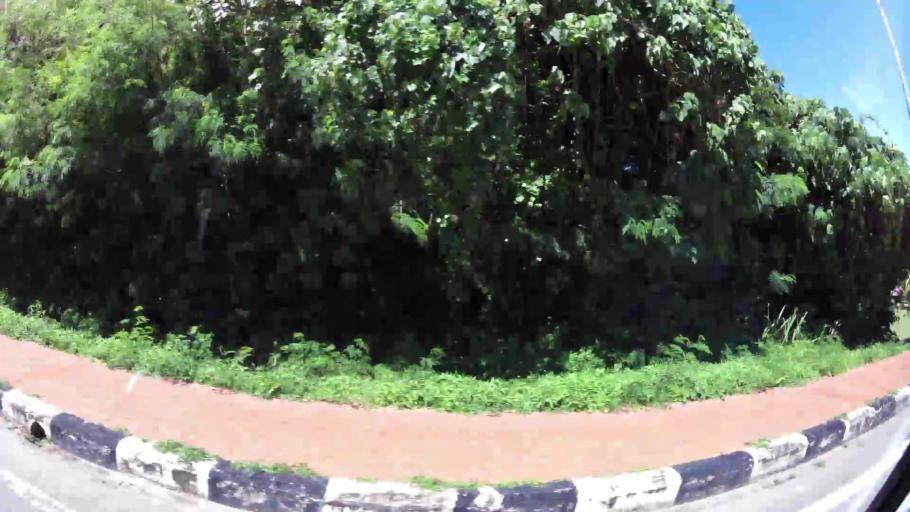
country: BN
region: Brunei and Muara
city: Bandar Seri Begawan
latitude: 5.0301
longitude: 115.0707
